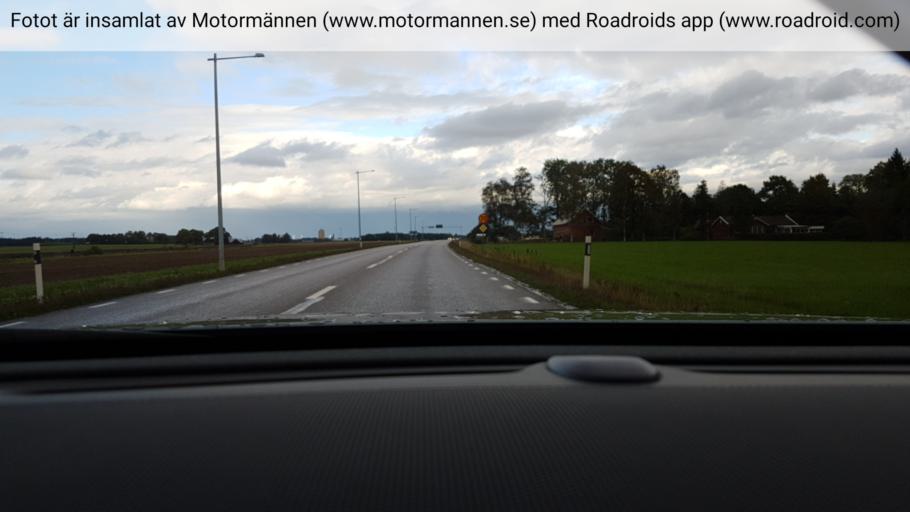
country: SE
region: Vaestra Goetaland
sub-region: Vanersborgs Kommun
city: Bralanda
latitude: 58.5351
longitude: 12.3222
